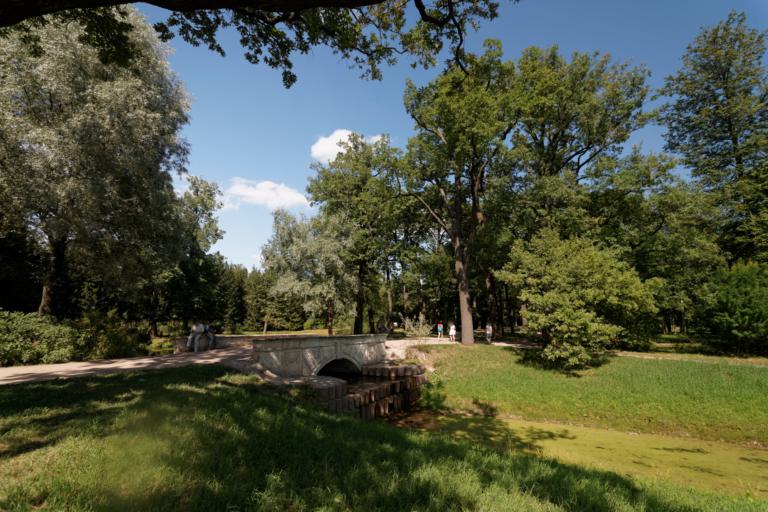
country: RU
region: St.-Petersburg
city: Pushkin
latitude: 59.7110
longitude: 30.3871
